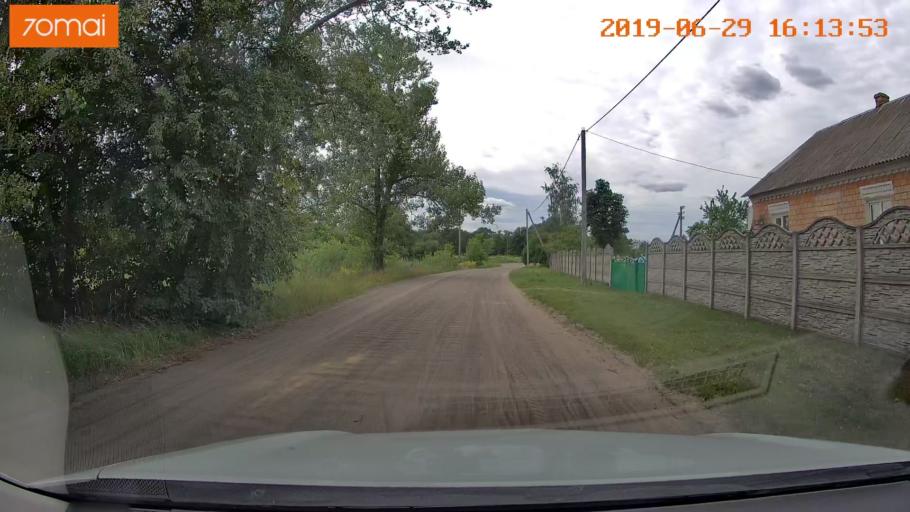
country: BY
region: Brest
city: Luninyets
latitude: 52.1990
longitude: 27.0188
